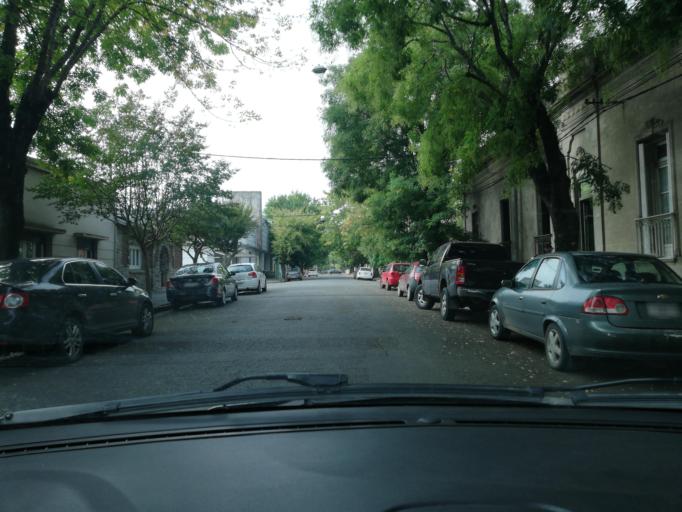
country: AR
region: Buenos Aires
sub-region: Partido de Balcarce
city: Balcarce
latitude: -37.8508
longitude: -58.2521
